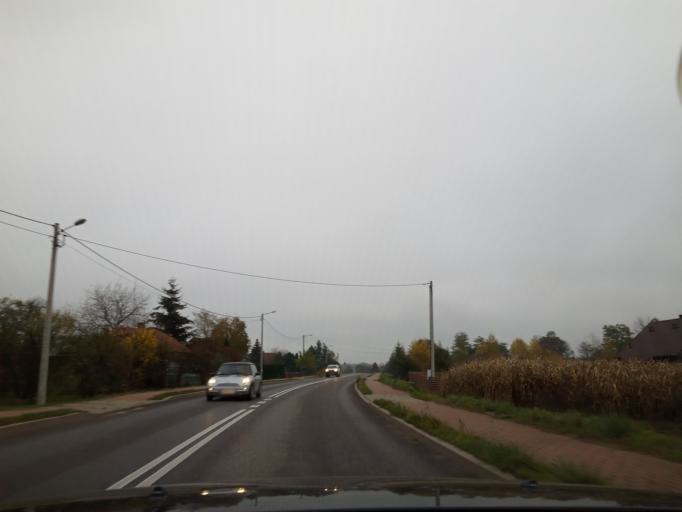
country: PL
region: Lesser Poland Voivodeship
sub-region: Powiat proszowicki
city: Klimontow
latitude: 50.2371
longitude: 20.3965
